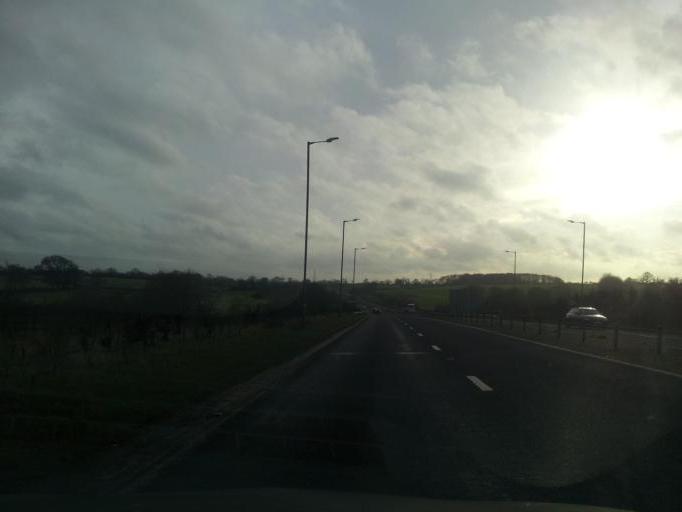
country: GB
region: England
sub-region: Central Bedfordshire
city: Leighton Buzzard
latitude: 51.9265
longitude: -0.6974
